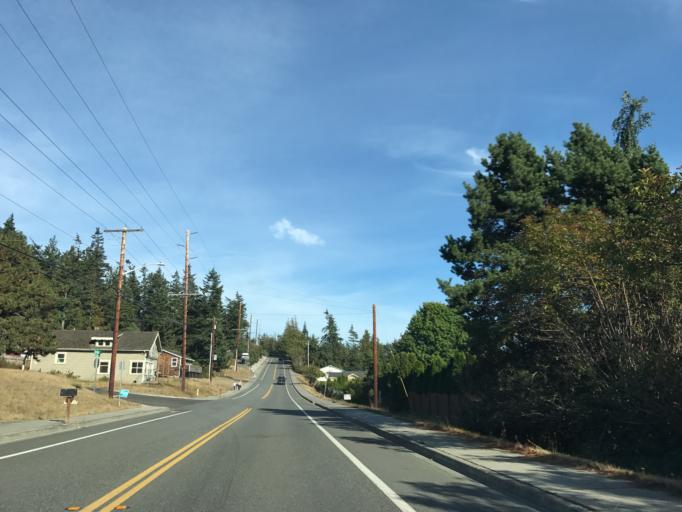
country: US
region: Washington
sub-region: Skagit County
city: Anacortes
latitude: 48.4988
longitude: -122.6833
